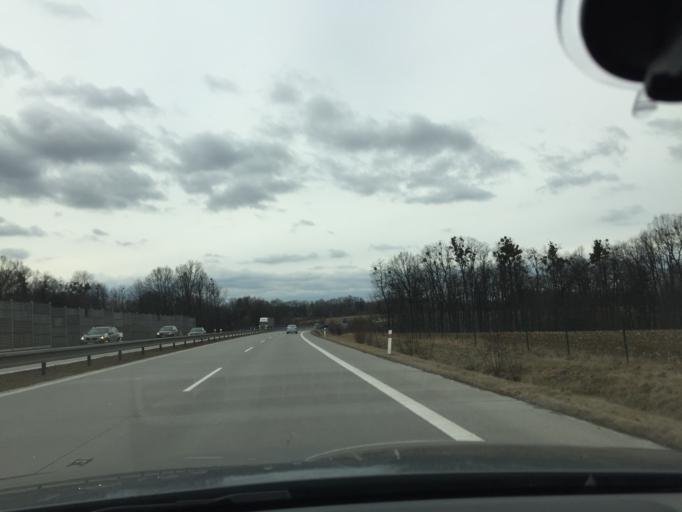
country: CZ
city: Dobratice
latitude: 49.6690
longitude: 18.4693
